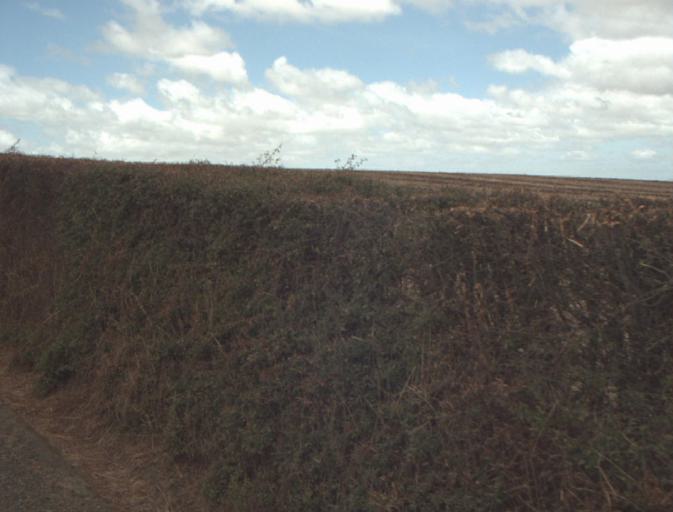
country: AU
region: Tasmania
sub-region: Northern Midlands
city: Evandale
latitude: -41.5214
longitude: 147.2634
